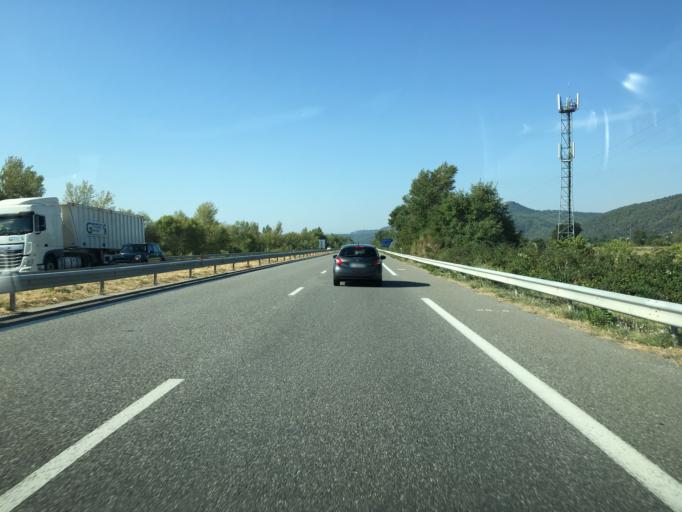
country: FR
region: Provence-Alpes-Cote d'Azur
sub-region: Departement des Alpes-de-Haute-Provence
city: Peyruis
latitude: 44.0324
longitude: 5.9594
